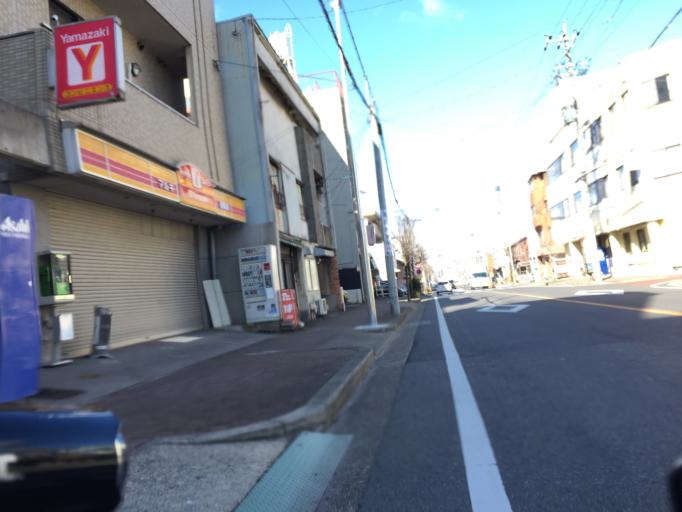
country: JP
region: Aichi
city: Nagoya-shi
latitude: 35.1618
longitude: 136.9421
